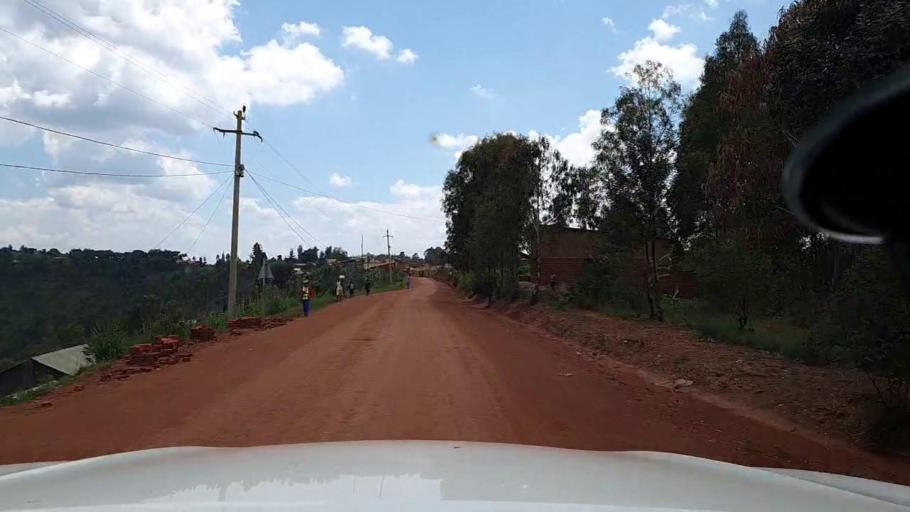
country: RW
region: Kigali
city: Kigali
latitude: -1.8020
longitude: 29.8426
